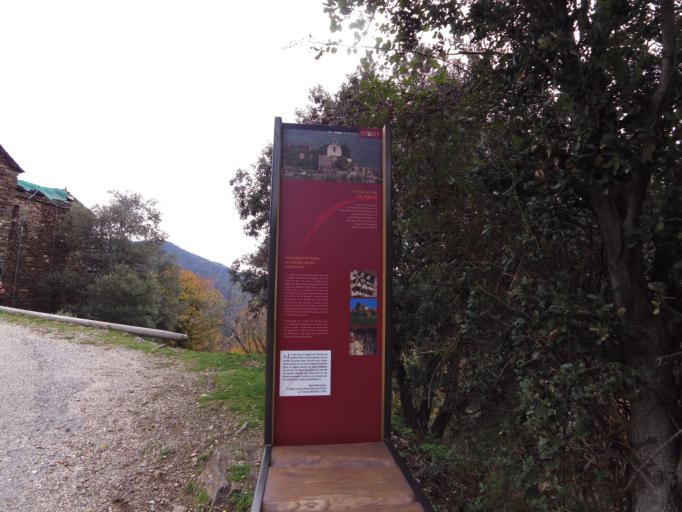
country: FR
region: Rhone-Alpes
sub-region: Departement de l'Ardeche
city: Les Vans
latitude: 44.4929
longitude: 4.0503
